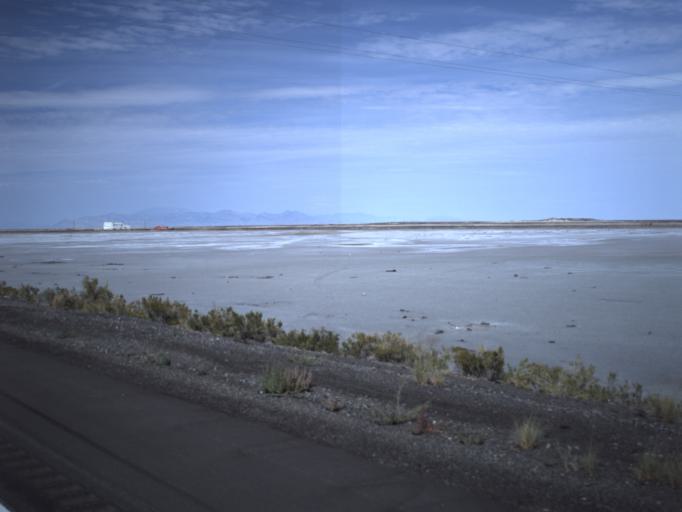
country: US
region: Utah
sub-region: Tooele County
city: Wendover
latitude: 40.7277
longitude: -113.2833
